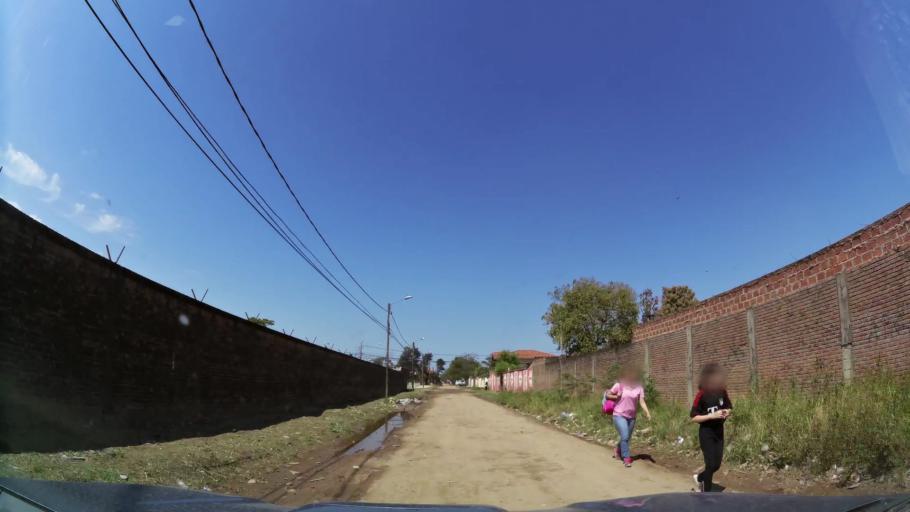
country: BO
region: Santa Cruz
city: Santa Cruz de la Sierra
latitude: -17.7325
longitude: -63.1508
